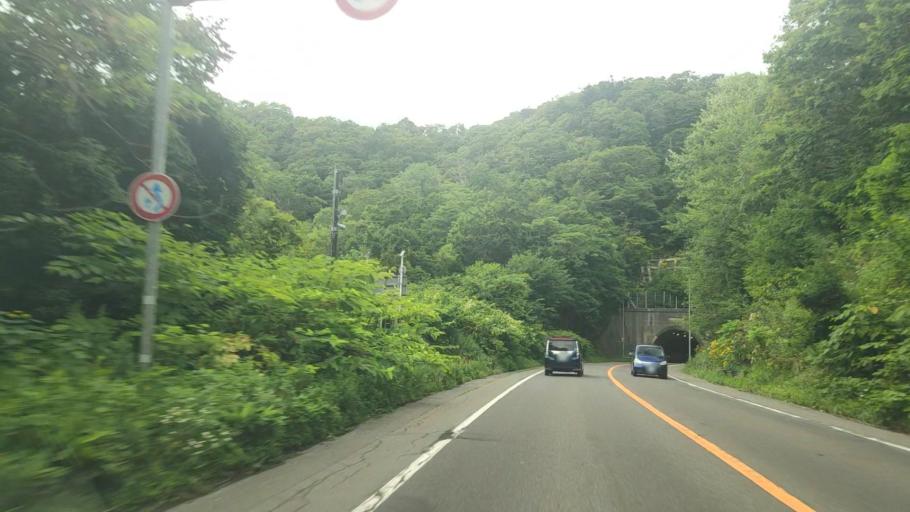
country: JP
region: Hokkaido
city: Niseko Town
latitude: 42.5909
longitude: 140.6756
